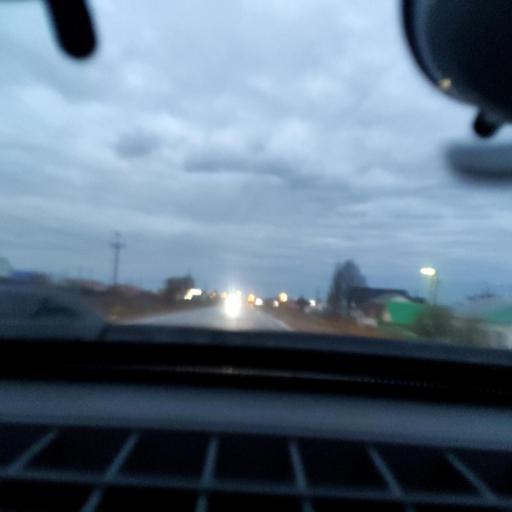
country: RU
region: Bashkortostan
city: Iglino
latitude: 54.7933
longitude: 56.2420
